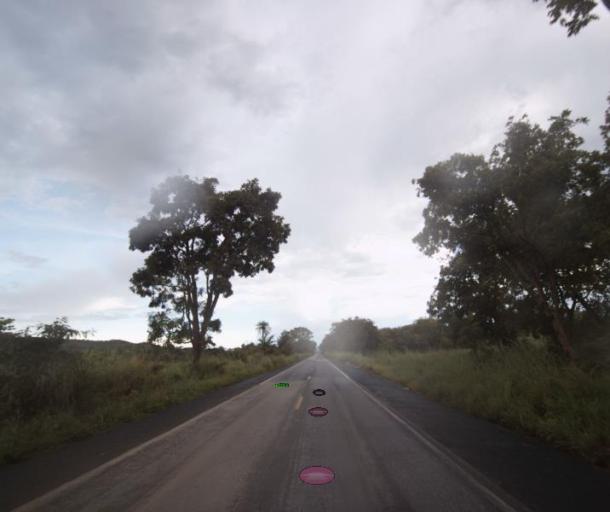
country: BR
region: Goias
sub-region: Porangatu
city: Porangatu
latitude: -13.9156
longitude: -49.0666
